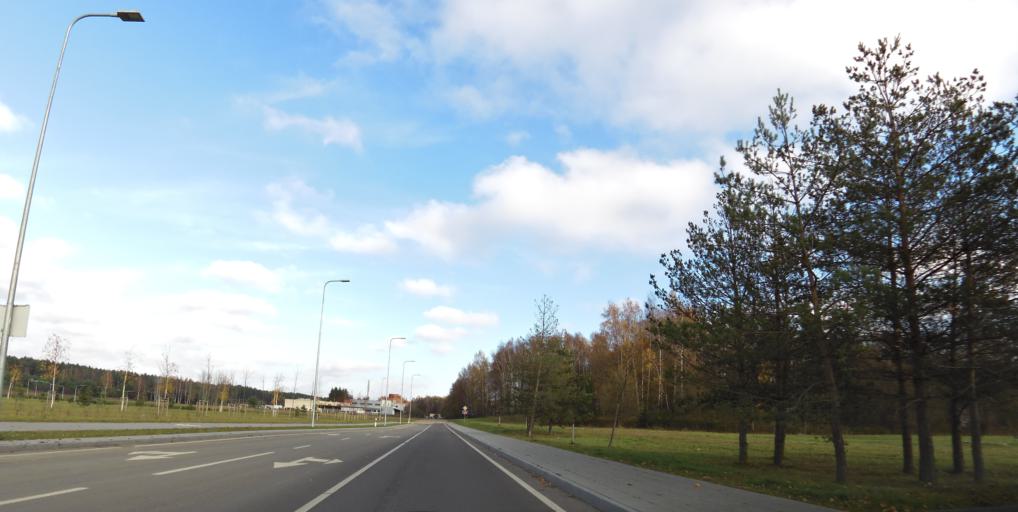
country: LT
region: Vilnius County
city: Lazdynai
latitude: 54.6831
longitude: 25.1960
